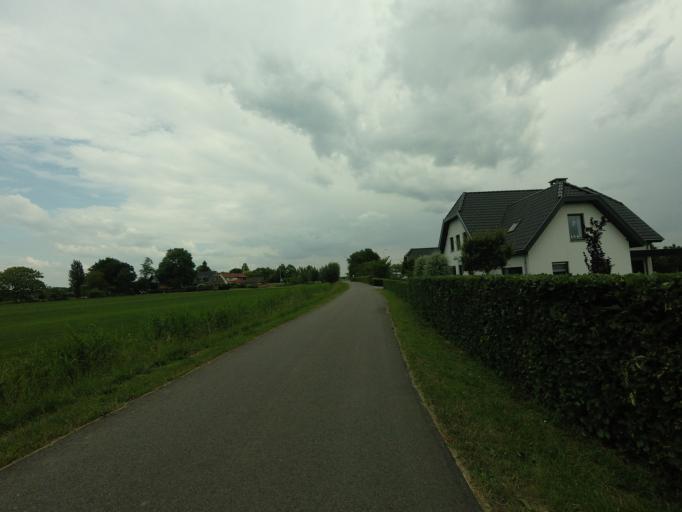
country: NL
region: Utrecht
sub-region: Gemeente Oudewater
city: Oudewater
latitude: 52.0245
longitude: 4.9037
